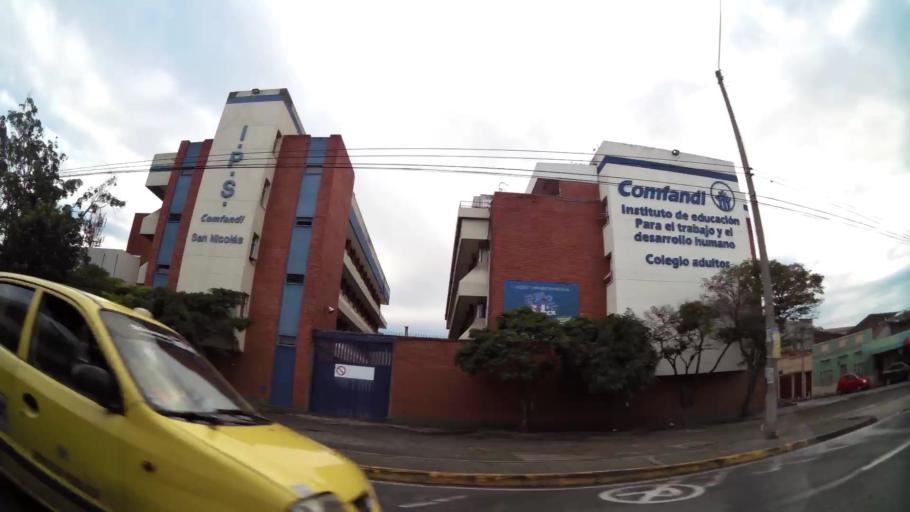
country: CO
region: Valle del Cauca
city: Cali
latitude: 3.4527
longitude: -76.5232
